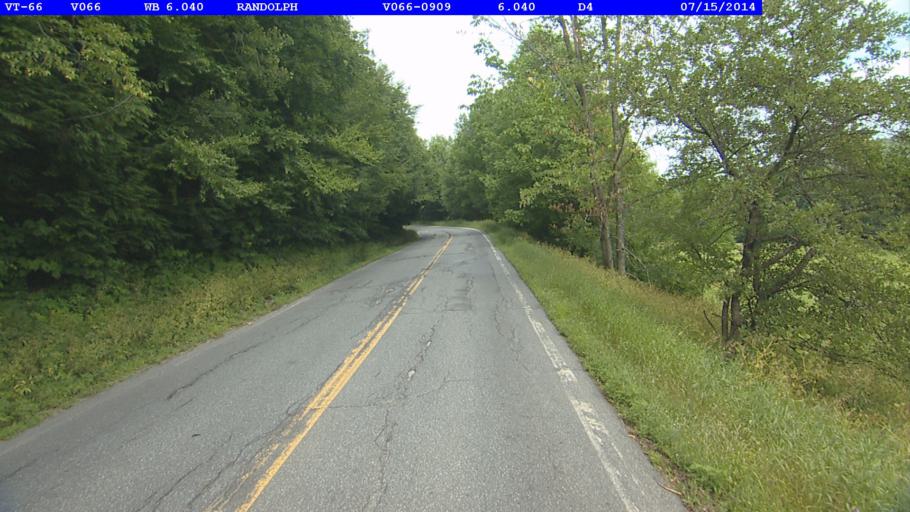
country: US
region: Vermont
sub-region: Orange County
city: Randolph
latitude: 43.9579
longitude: -72.5710
